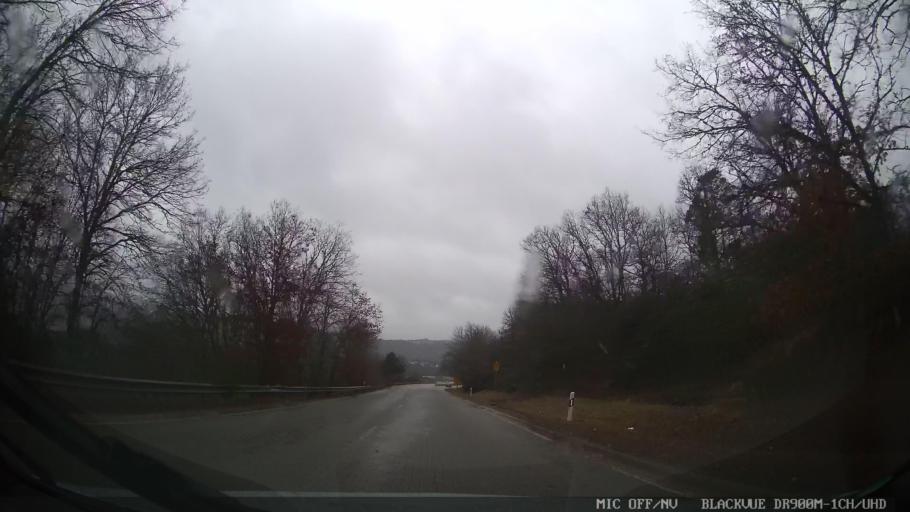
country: DE
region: Rheinland-Pfalz
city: Idar-Oberstein
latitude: 49.7042
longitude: 7.2974
